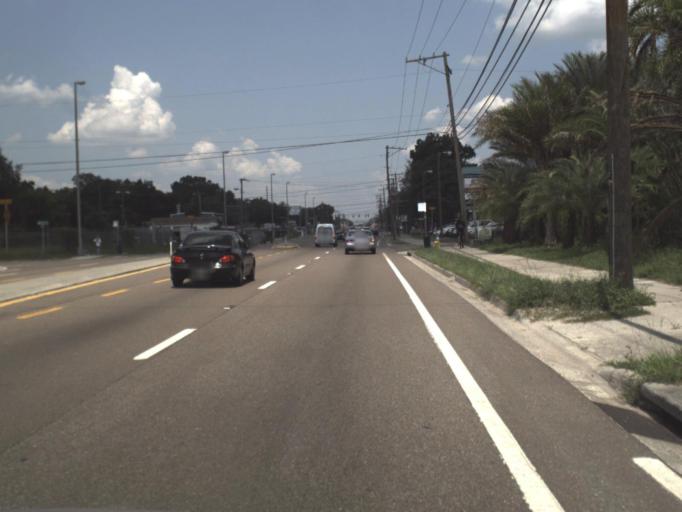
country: US
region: Florida
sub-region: Hillsborough County
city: University
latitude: 28.0621
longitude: -82.4511
